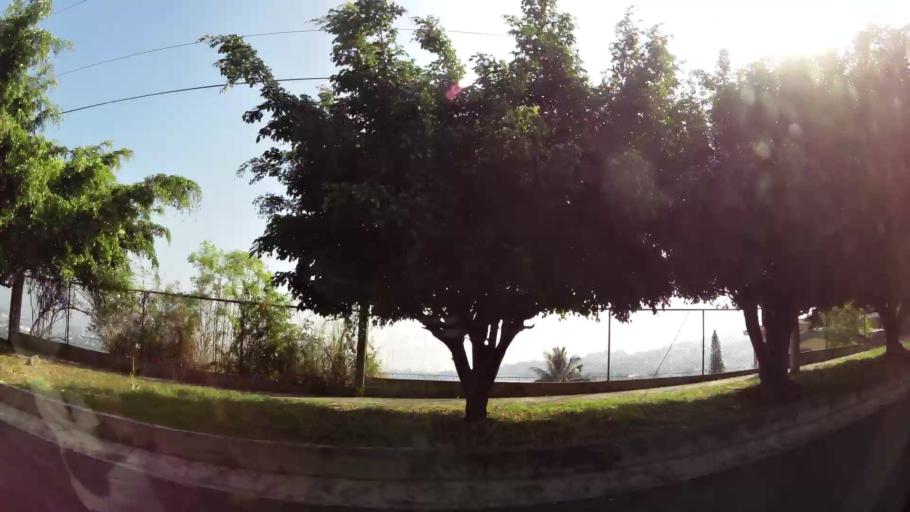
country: SV
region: La Libertad
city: Antiguo Cuscatlan
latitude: 13.6808
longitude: -89.2302
